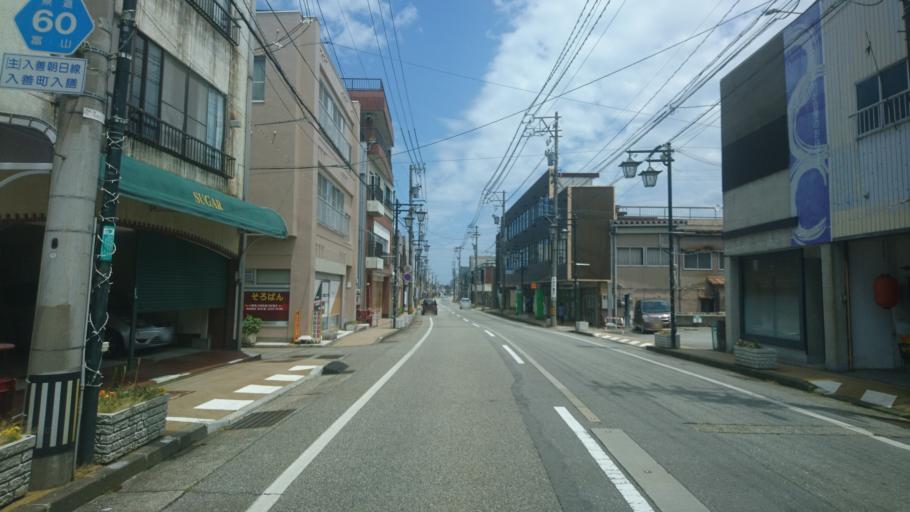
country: JP
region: Toyama
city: Nyuzen
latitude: 36.9399
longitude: 137.5014
